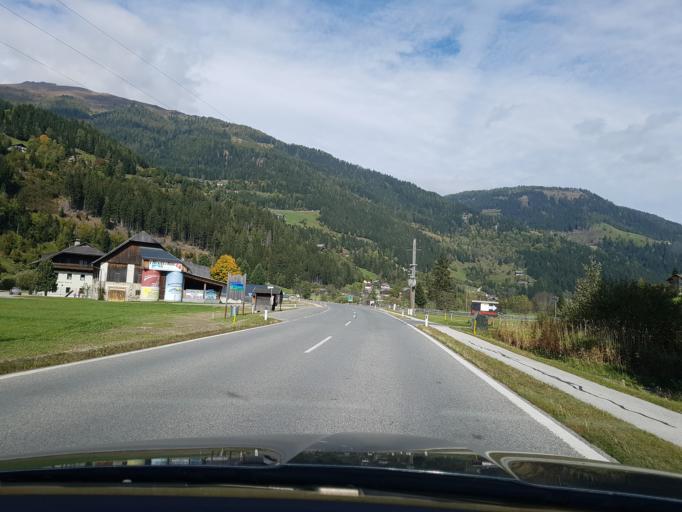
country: AT
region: Carinthia
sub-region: Politischer Bezirk Spittal an der Drau
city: Kleinkirchheim
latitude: 46.8223
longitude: 13.8620
